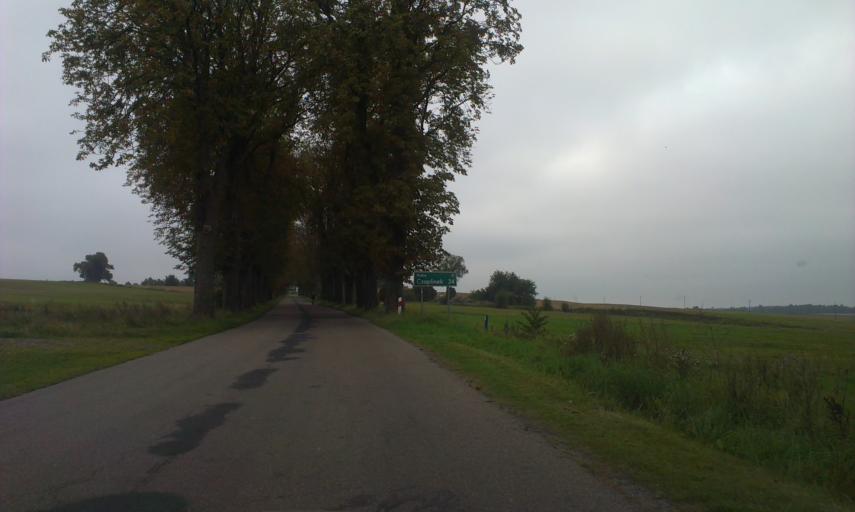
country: PL
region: West Pomeranian Voivodeship
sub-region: Powiat szczecinecki
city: Barwice
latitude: 53.7350
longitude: 16.3549
